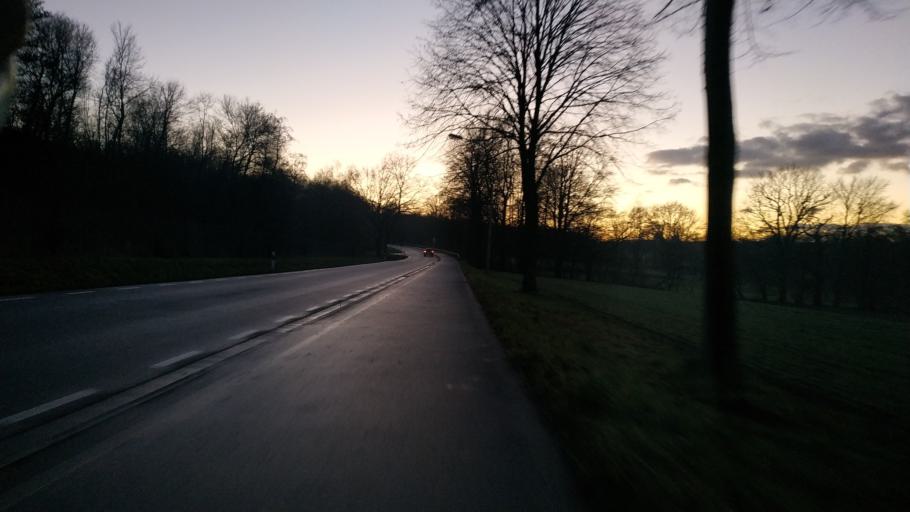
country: DE
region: North Rhine-Westphalia
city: Ibbenburen
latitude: 52.2940
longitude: 7.7378
